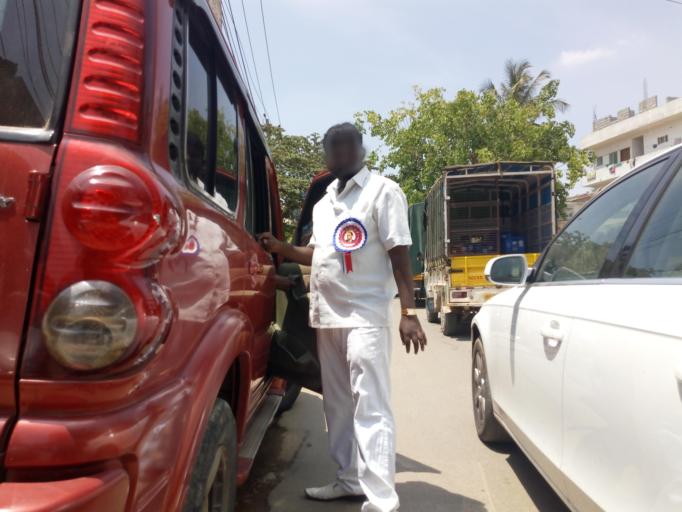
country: IN
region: Karnataka
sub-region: Bangalore Urban
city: Bangalore
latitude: 12.8879
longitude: 77.6565
